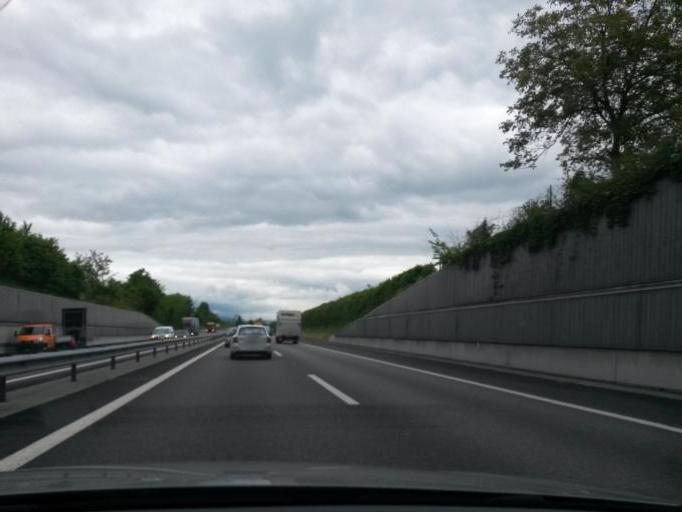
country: CH
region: Aargau
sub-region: Bezirk Zofingen
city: Brittnau
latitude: 47.2599
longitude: 7.9493
